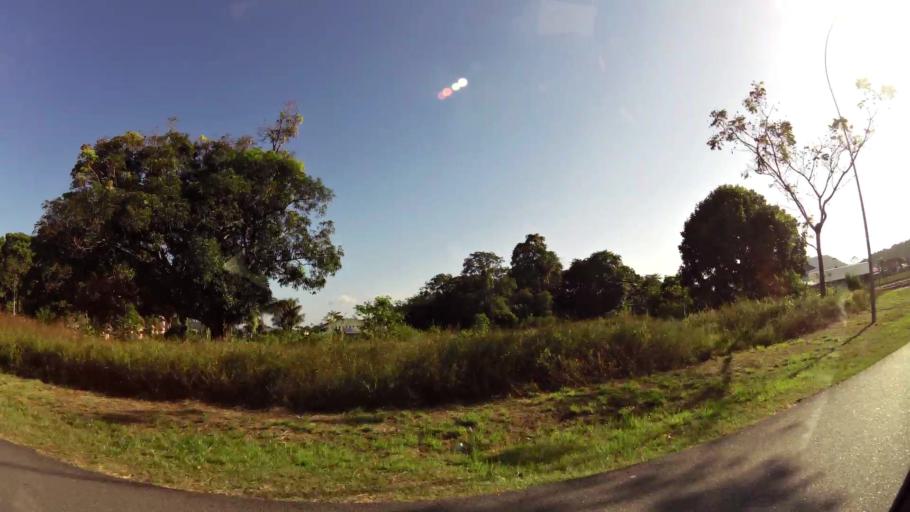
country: GF
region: Guyane
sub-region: Guyane
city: Remire-Montjoly
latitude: 4.9007
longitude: -52.2748
